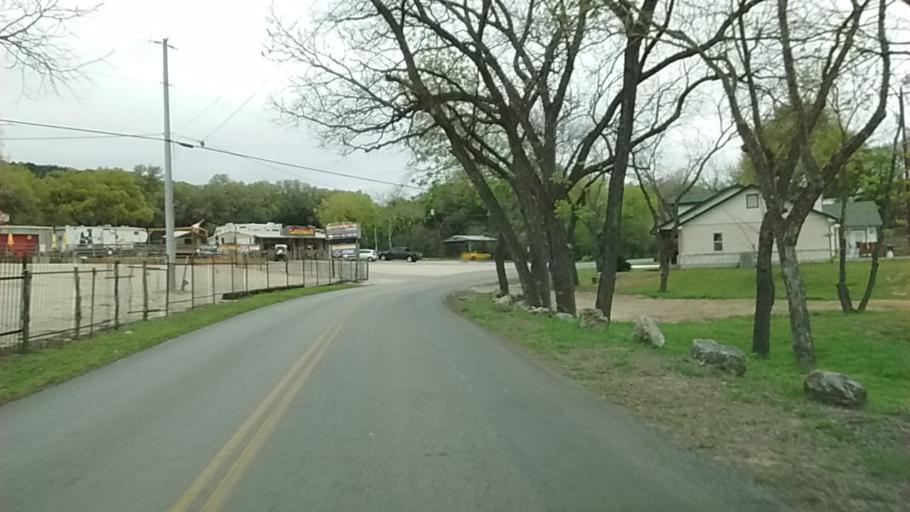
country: US
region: Texas
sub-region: Comal County
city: New Braunfels
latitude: 29.7987
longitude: -98.1488
